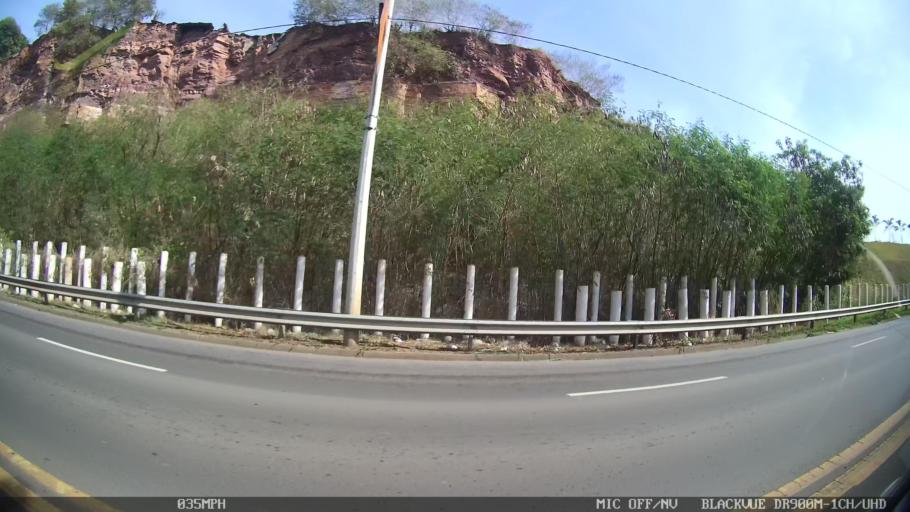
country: BR
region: Sao Paulo
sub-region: Piracicaba
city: Piracicaba
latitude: -22.7130
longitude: -47.6778
